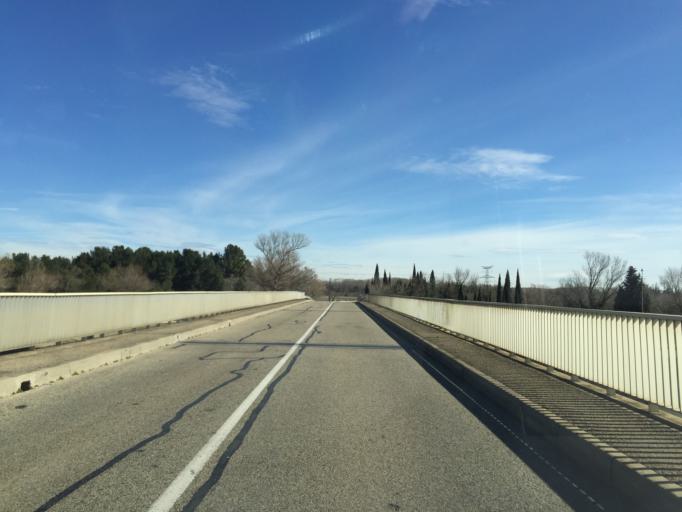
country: FR
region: Languedoc-Roussillon
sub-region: Departement du Gard
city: Saint-Genies-de-Comolas
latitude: 44.1102
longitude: 4.7112
